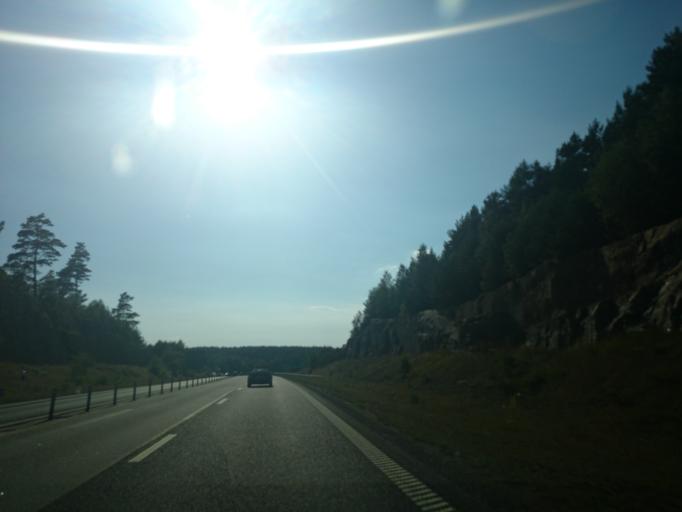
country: SE
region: Blekinge
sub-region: Ronneby Kommun
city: Ronneby
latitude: 56.2303
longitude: 15.2482
